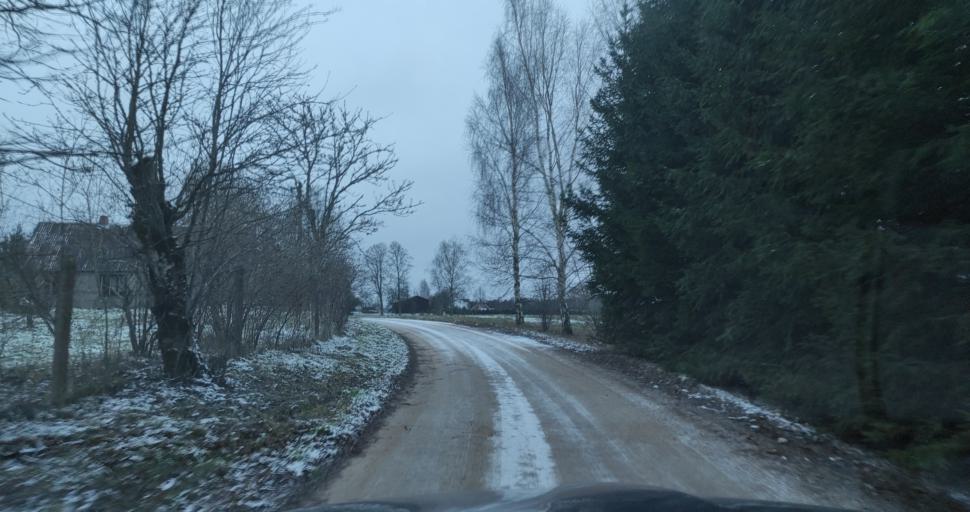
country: LV
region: Kuldigas Rajons
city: Kuldiga
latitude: 56.9764
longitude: 22.0539
